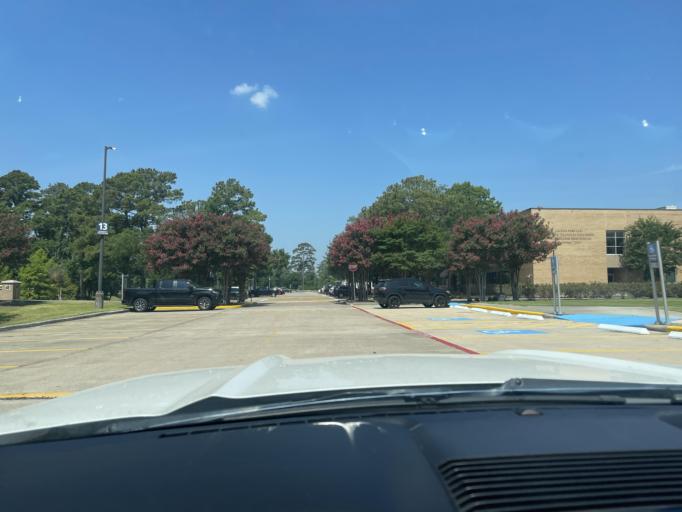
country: US
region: Texas
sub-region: Harris County
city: Cloverleaf
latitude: 29.8092
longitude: -95.1802
